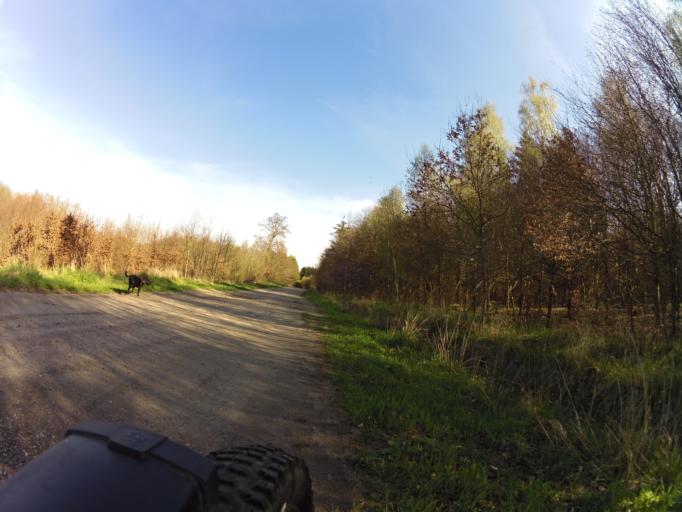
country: PL
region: West Pomeranian Voivodeship
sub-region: Powiat lobeski
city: Lobez
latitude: 53.7731
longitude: 15.5805
